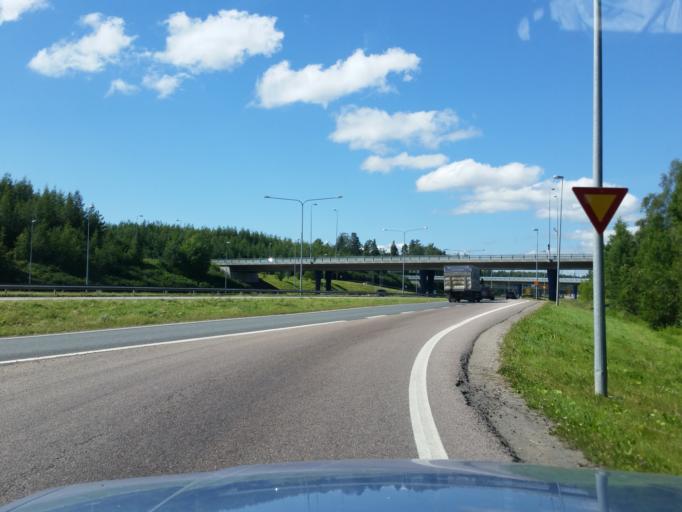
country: FI
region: Uusimaa
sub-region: Helsinki
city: Kauniainen
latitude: 60.2054
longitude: 24.7486
